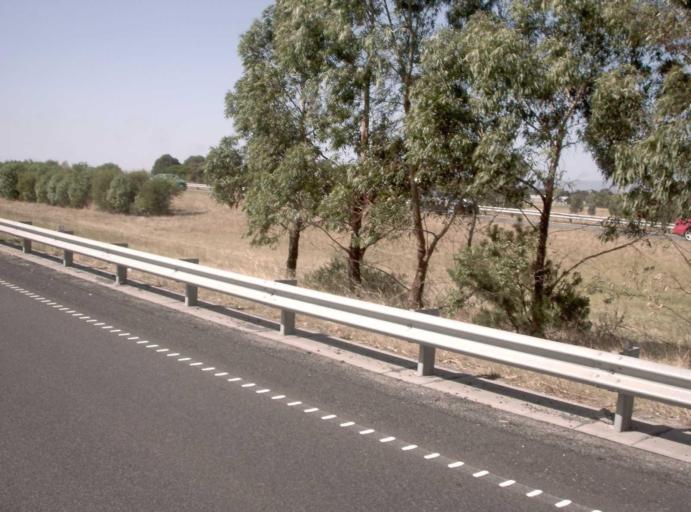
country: AU
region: Victoria
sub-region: Kingston
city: Chelsea Heights
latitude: -38.0455
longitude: 145.1421
